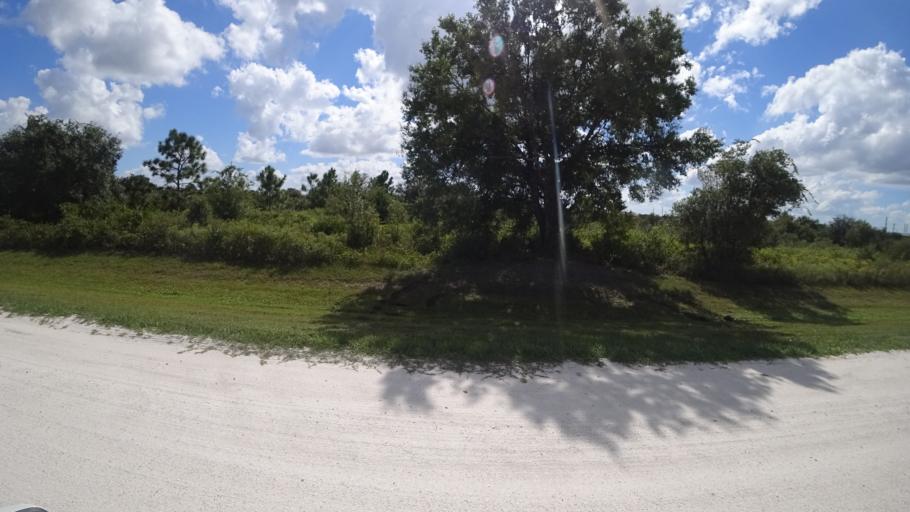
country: US
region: Florida
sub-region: Sarasota County
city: The Meadows
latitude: 27.4376
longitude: -82.3868
